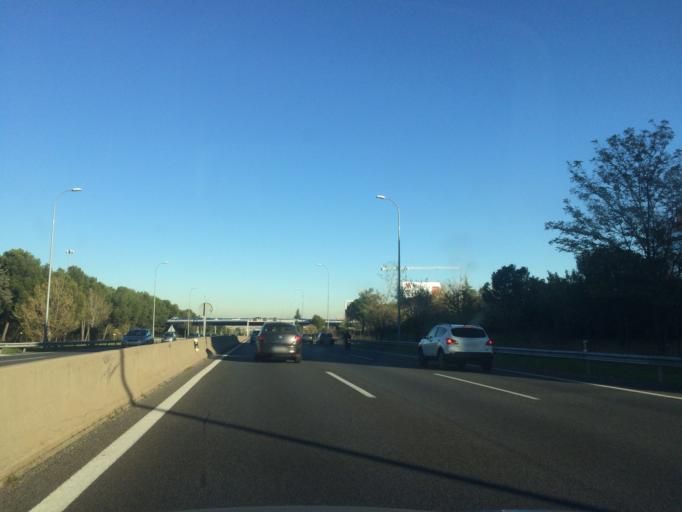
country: ES
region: Madrid
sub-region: Provincia de Madrid
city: San Blas
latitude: 40.4494
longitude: -3.6296
